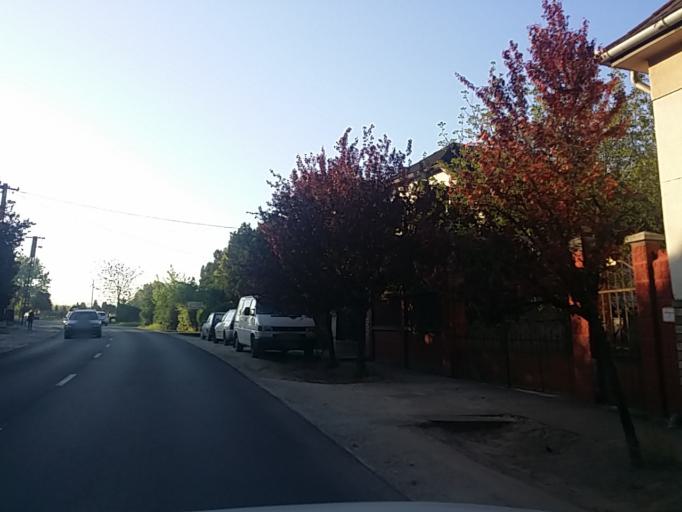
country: HU
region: Pest
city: Fot
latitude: 47.6047
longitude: 19.2041
